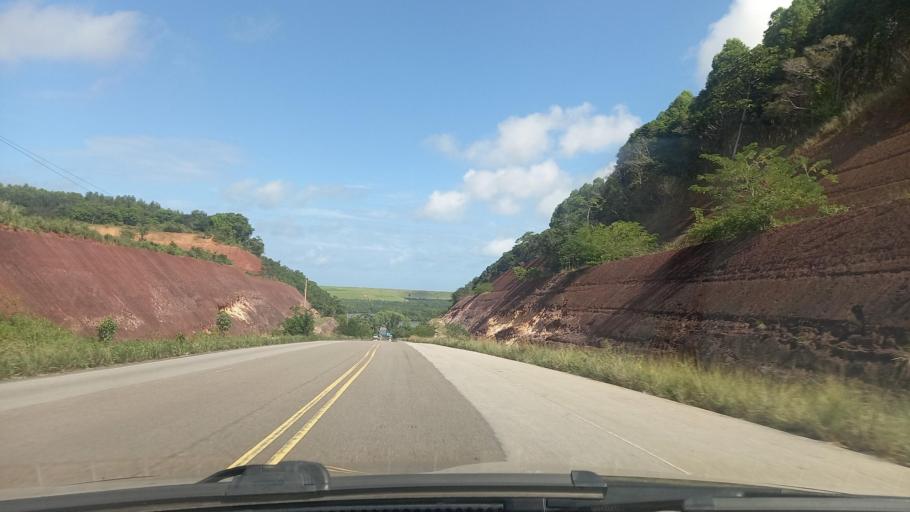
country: BR
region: Alagoas
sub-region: Marechal Deodoro
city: Marechal Deodoro
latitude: -9.8309
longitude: -35.9294
